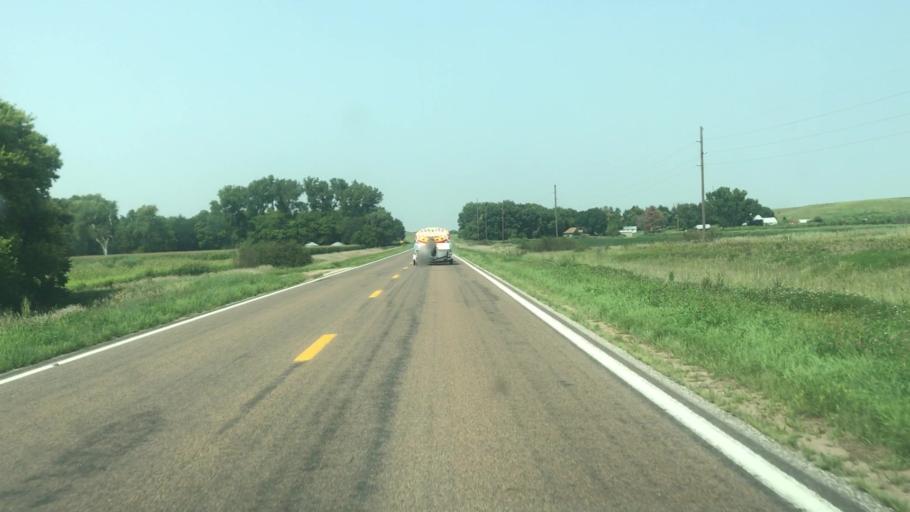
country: US
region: Nebraska
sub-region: Sherman County
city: Loup City
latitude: 41.2456
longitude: -98.9387
